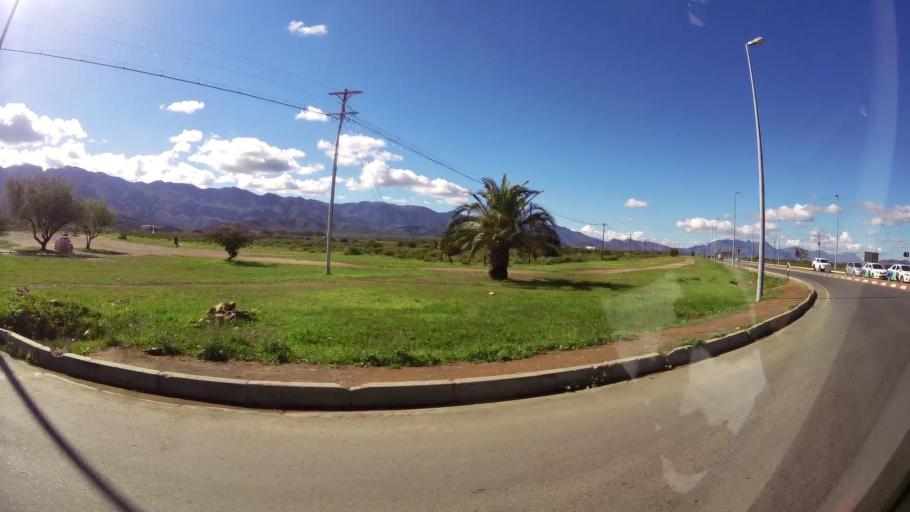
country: ZA
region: Western Cape
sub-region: Cape Winelands District Municipality
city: Ashton
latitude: -33.8147
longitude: 19.8979
